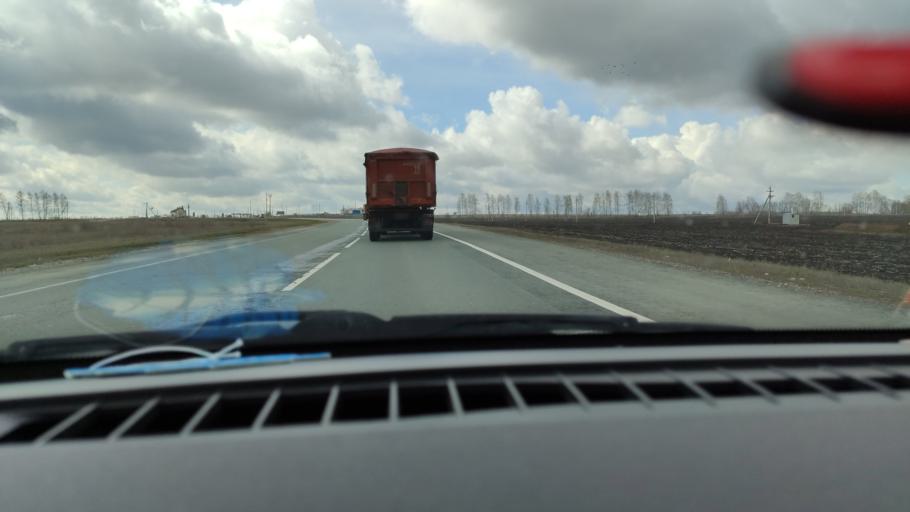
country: RU
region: Samara
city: Yelkhovka
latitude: 53.8755
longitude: 50.2577
